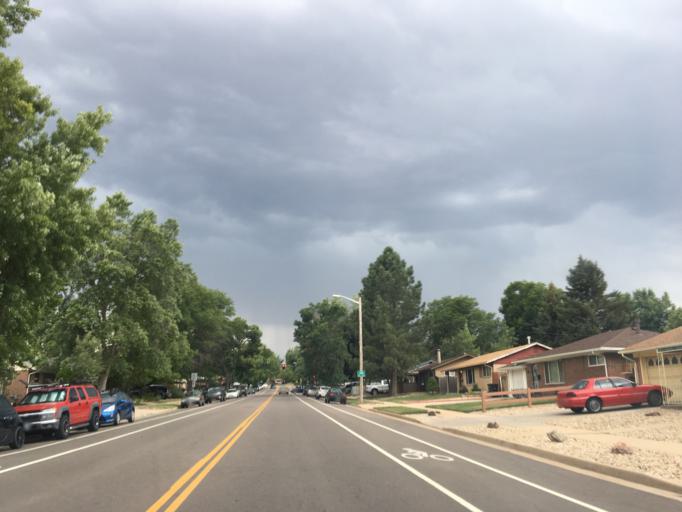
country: US
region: Colorado
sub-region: Arapahoe County
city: Sheridan
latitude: 39.6690
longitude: -105.0350
